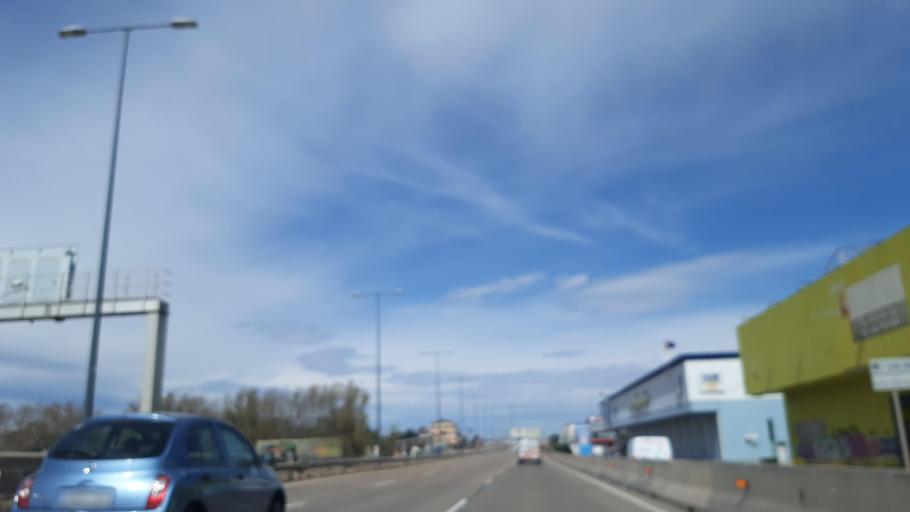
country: ES
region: Aragon
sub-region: Provincia de Zaragoza
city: Oliver-Valdefierro, Oliver, Valdefierro
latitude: 41.6772
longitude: -0.9587
